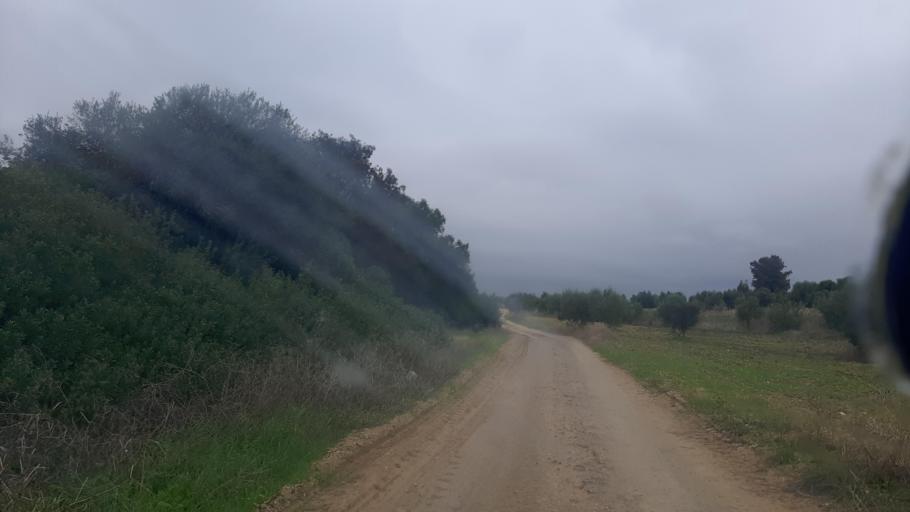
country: TN
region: Tunis
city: La Sebala du Mornag
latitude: 36.5753
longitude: 10.2921
